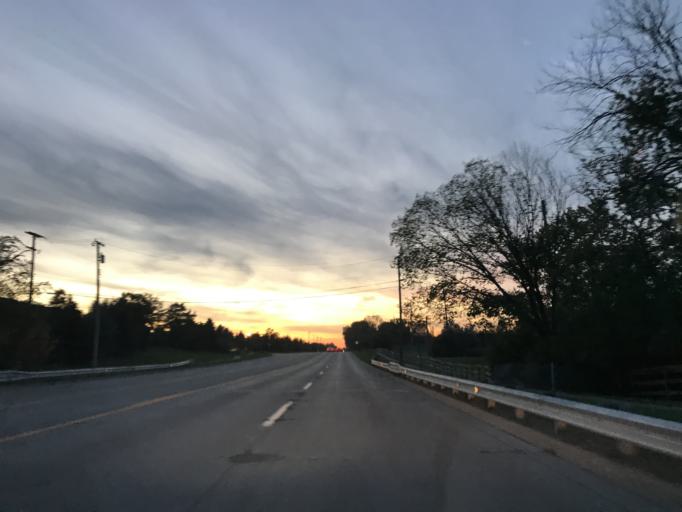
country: US
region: Michigan
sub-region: Oakland County
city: Farmington
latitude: 42.4400
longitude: -83.3991
